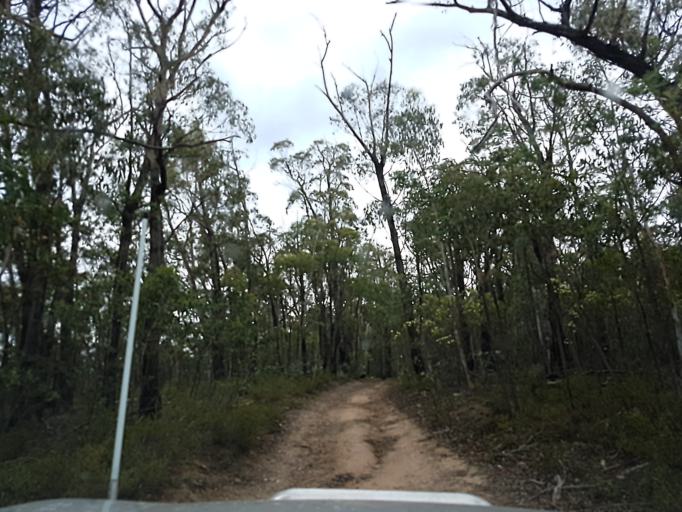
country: AU
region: New South Wales
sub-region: Snowy River
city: Jindabyne
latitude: -36.8573
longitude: 148.3320
